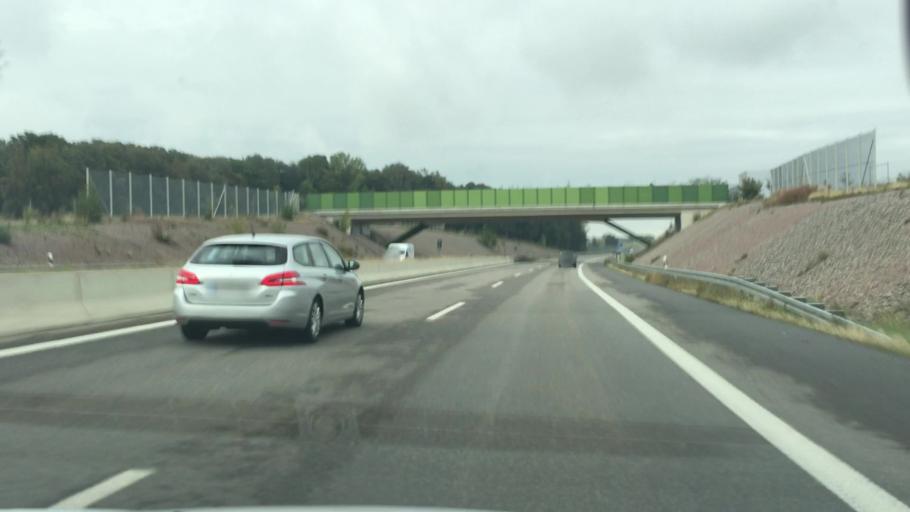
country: DE
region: Saxony
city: Narsdorf
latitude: 51.0147
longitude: 12.6829
